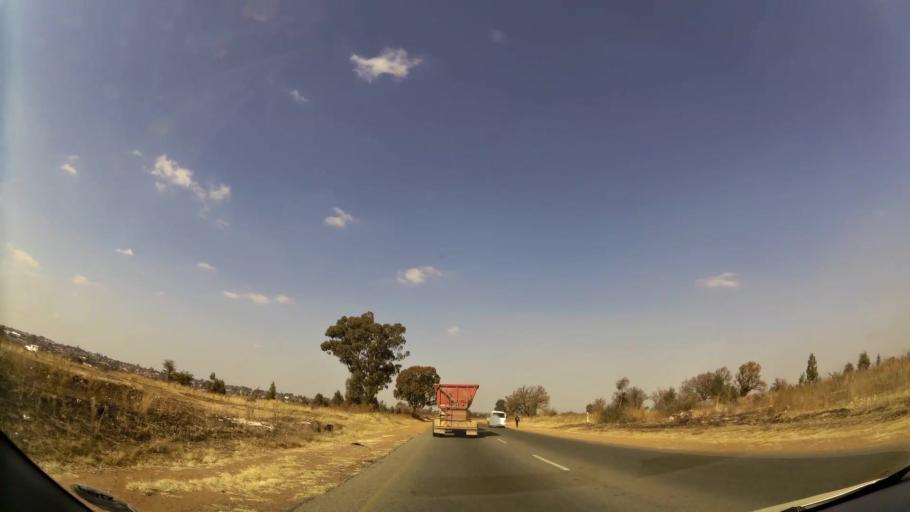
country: ZA
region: Gauteng
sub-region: West Rand District Municipality
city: Krugersdorp
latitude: -26.1309
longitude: 27.8154
